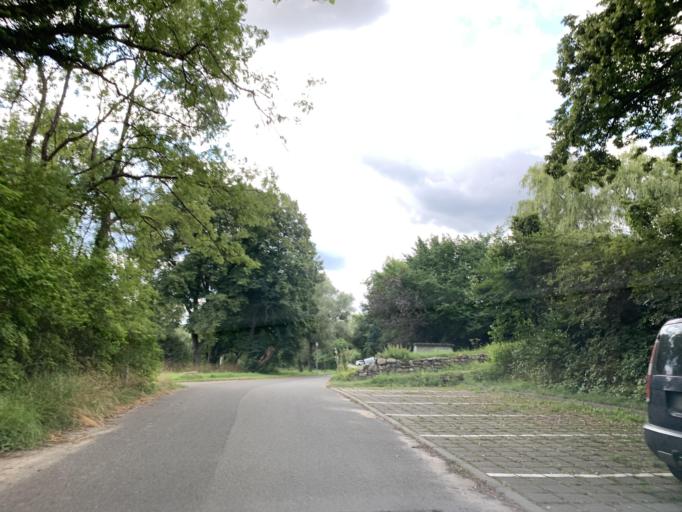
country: DE
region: Mecklenburg-Vorpommern
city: Carpin
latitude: 53.4058
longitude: 13.1997
